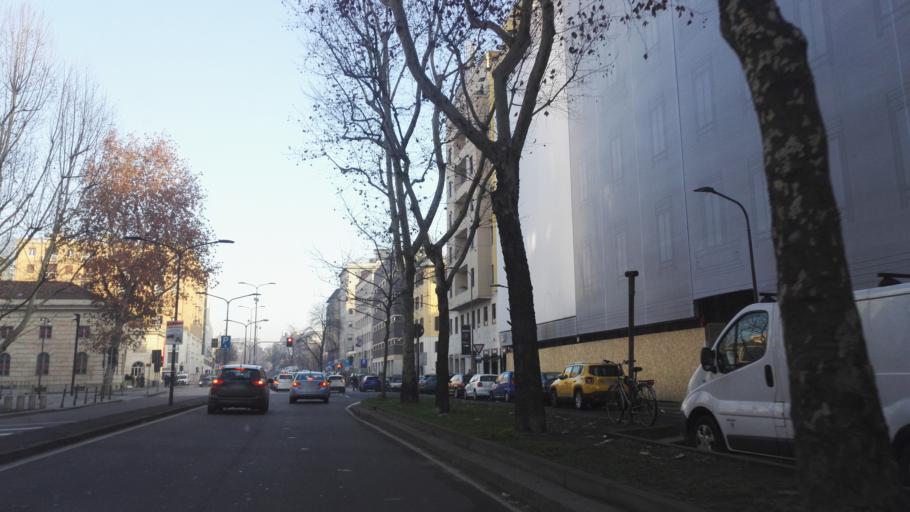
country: IT
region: Lombardy
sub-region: Citta metropolitana di Milano
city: Milano
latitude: 45.4807
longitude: 9.1854
